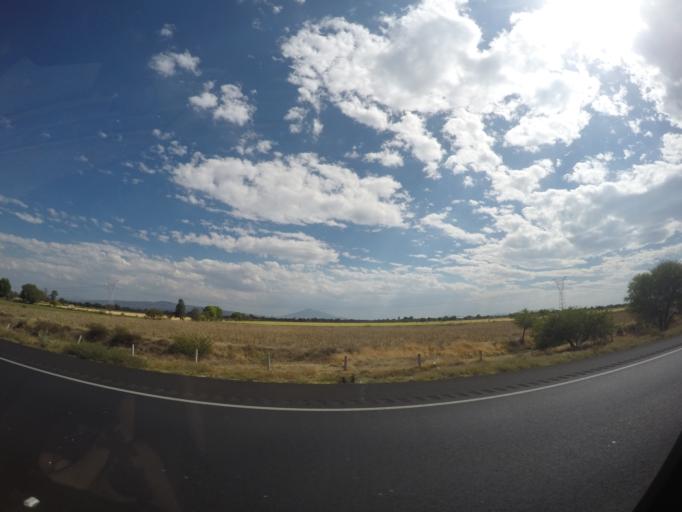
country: MX
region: Guanajuato
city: Santiago de Cuenda
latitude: 20.5785
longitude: -100.9685
